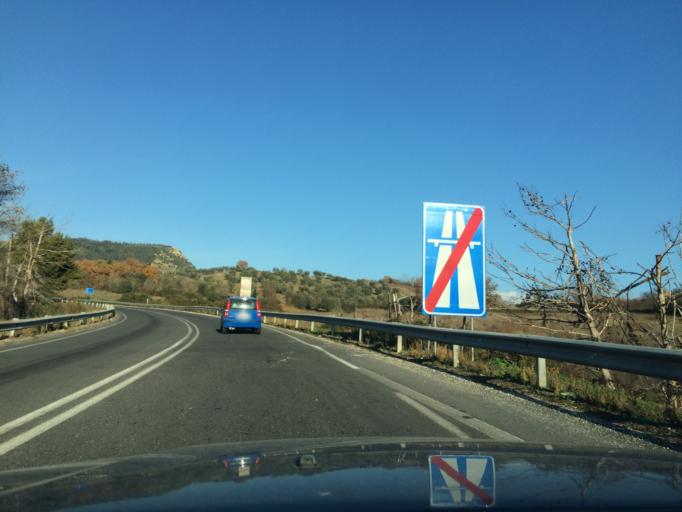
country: IT
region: Umbria
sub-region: Provincia di Terni
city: Fornole
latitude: 42.5321
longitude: 12.4748
